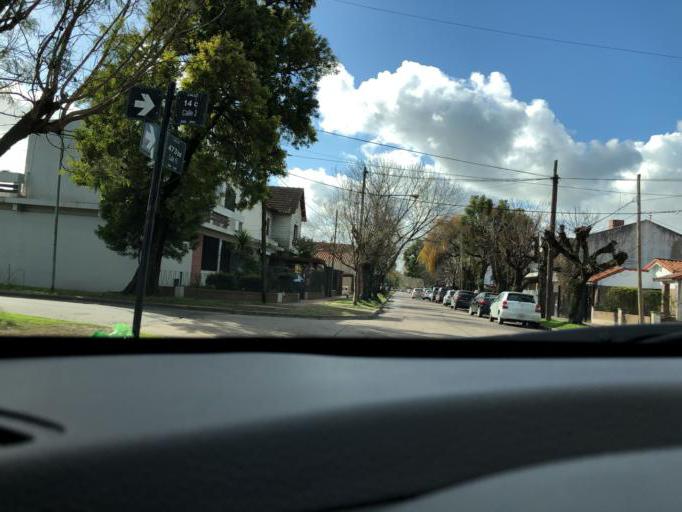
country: AR
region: Buenos Aires
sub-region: Partido de La Plata
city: La Plata
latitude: -34.8732
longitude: -58.0460
